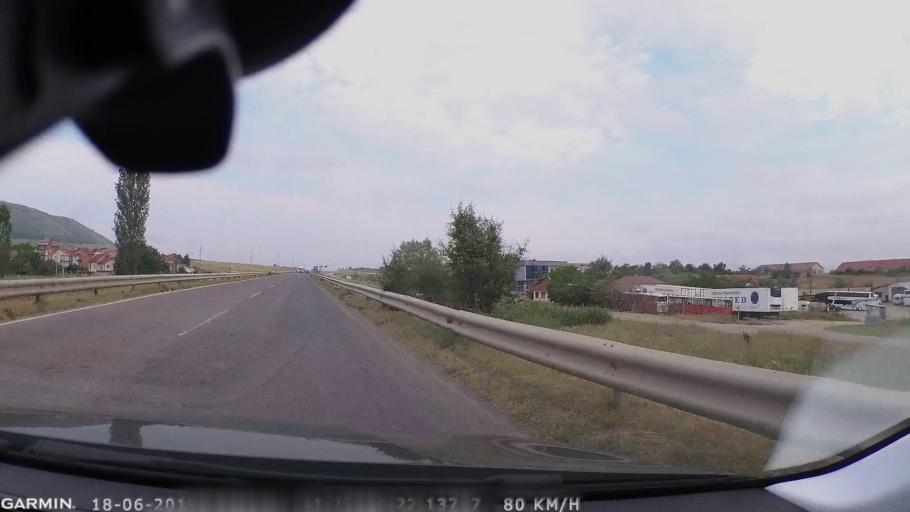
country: MK
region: Stip
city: Shtip
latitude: 41.7752
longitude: 22.1369
